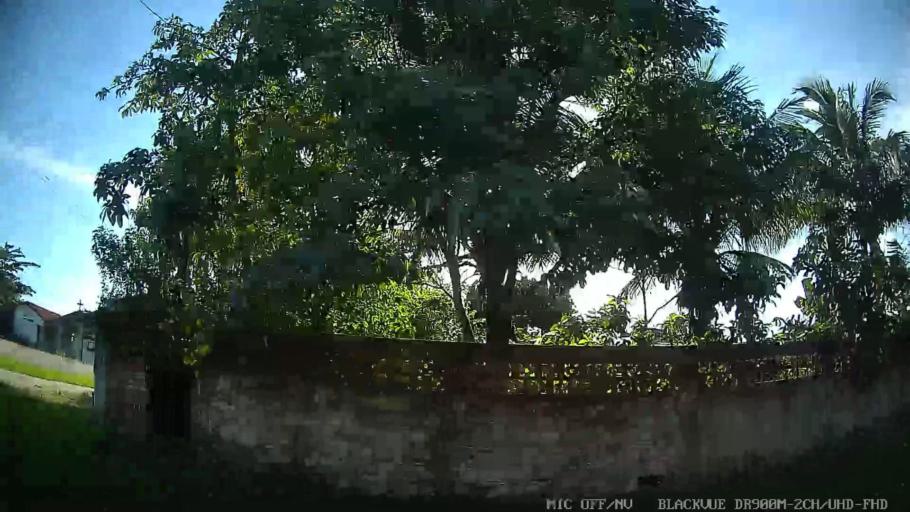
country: BR
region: Sao Paulo
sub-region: Iguape
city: Iguape
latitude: -24.7573
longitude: -47.5742
